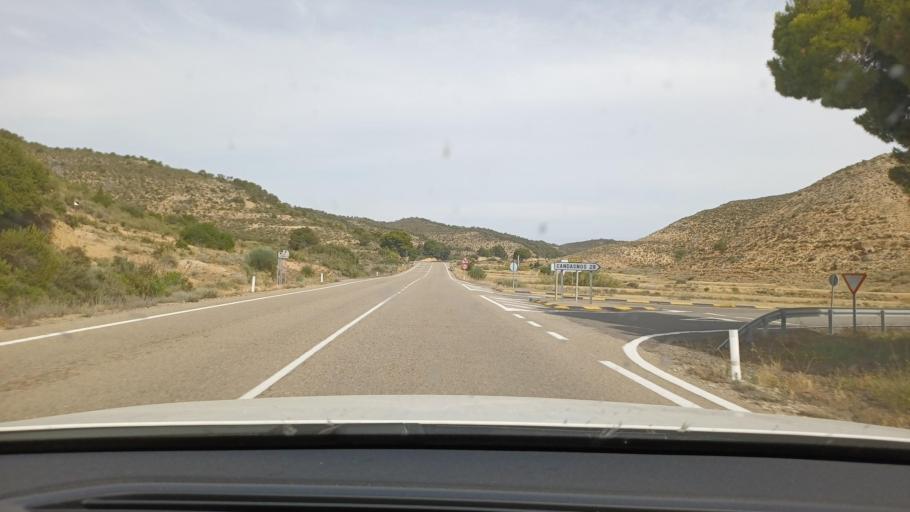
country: ES
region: Aragon
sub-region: Provincia de Zaragoza
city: Chiprana
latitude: 41.3459
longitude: -0.0878
